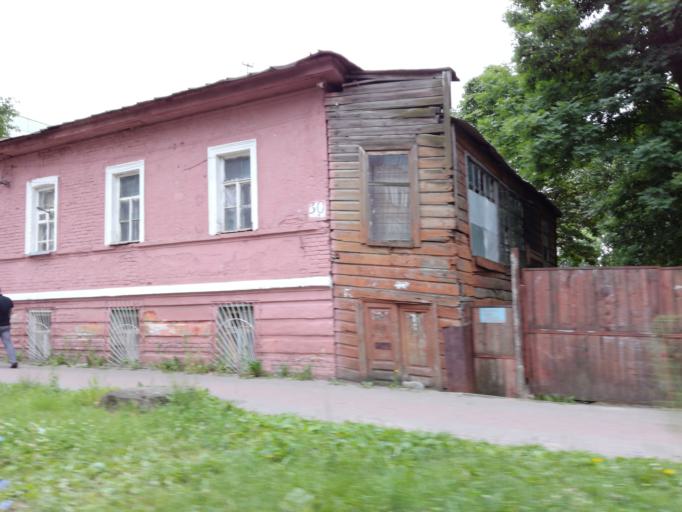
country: RU
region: Kursk
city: Kursk
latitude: 51.7419
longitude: 36.1889
